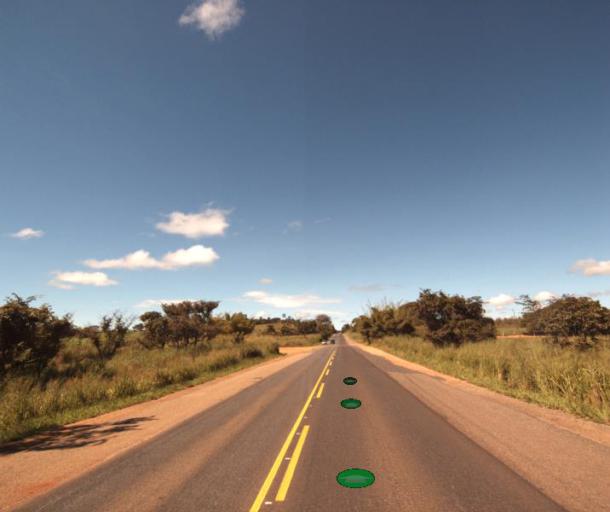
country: BR
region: Goias
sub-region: Ceres
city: Ceres
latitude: -15.1830
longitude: -49.5450
